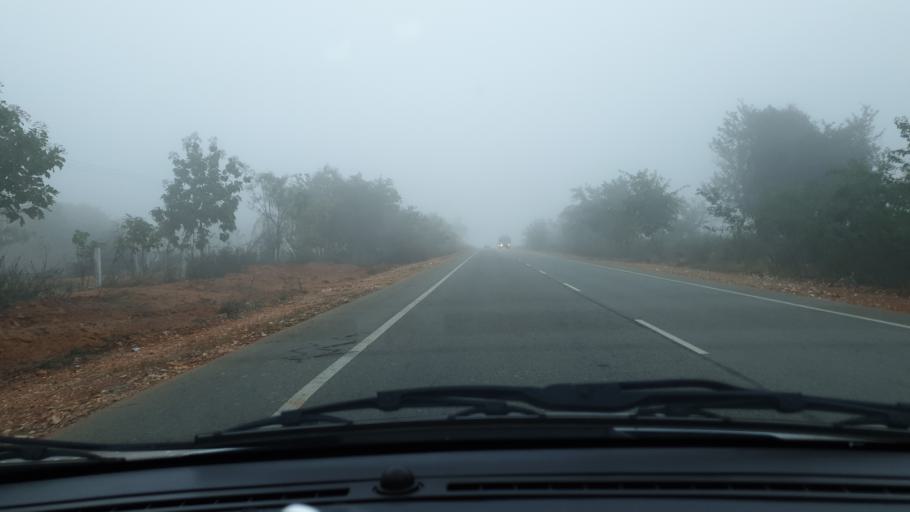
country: IN
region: Telangana
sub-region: Mahbubnagar
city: Nagar Karnul
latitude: 16.6384
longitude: 78.5967
